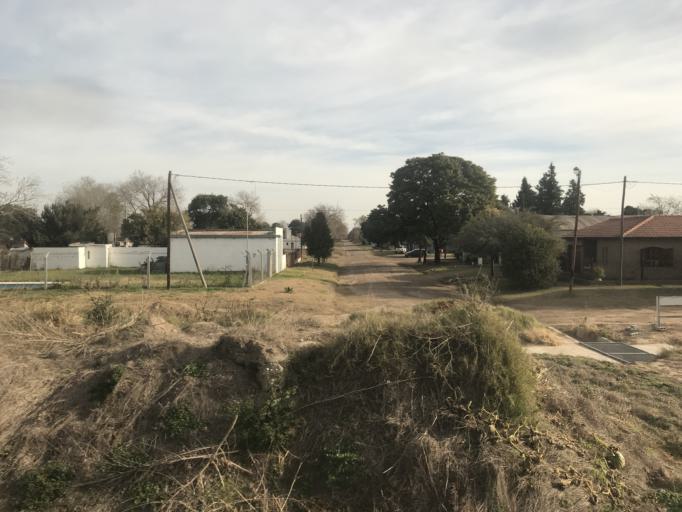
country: AR
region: Cordoba
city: Pilar
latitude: -31.6866
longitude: -63.8818
